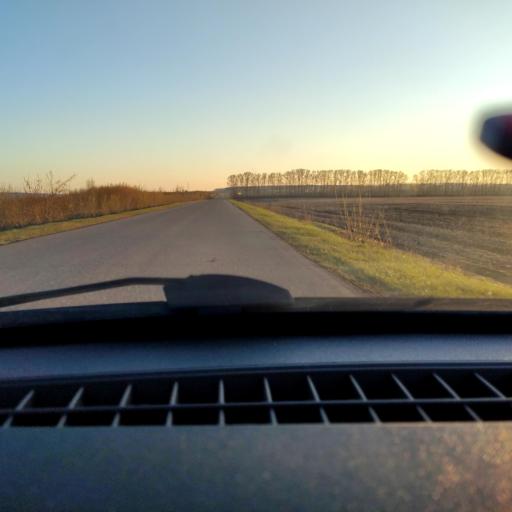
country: RU
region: Bashkortostan
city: Avdon
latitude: 54.5325
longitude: 55.6421
